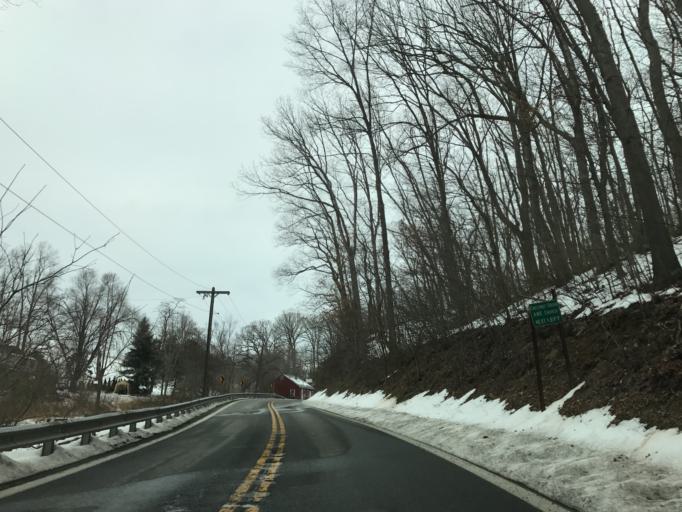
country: US
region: Maryland
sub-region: Harford County
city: Jarrettsville
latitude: 39.6492
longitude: -76.4103
